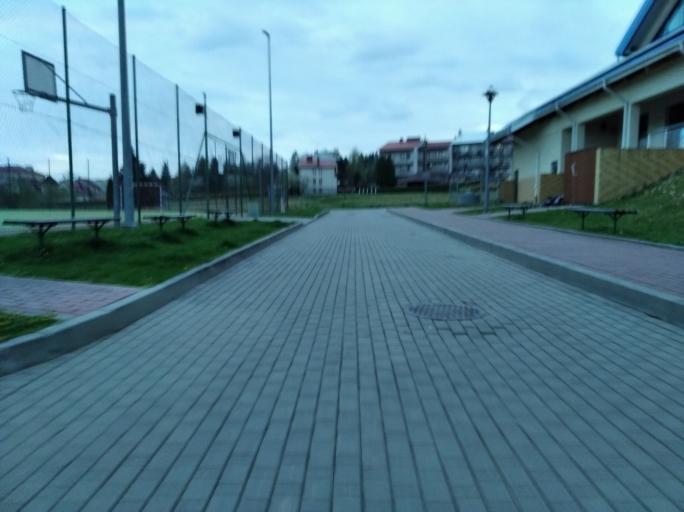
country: PL
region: Subcarpathian Voivodeship
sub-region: Powiat strzyzowski
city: Strzyzow
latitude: 49.8723
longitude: 21.7907
